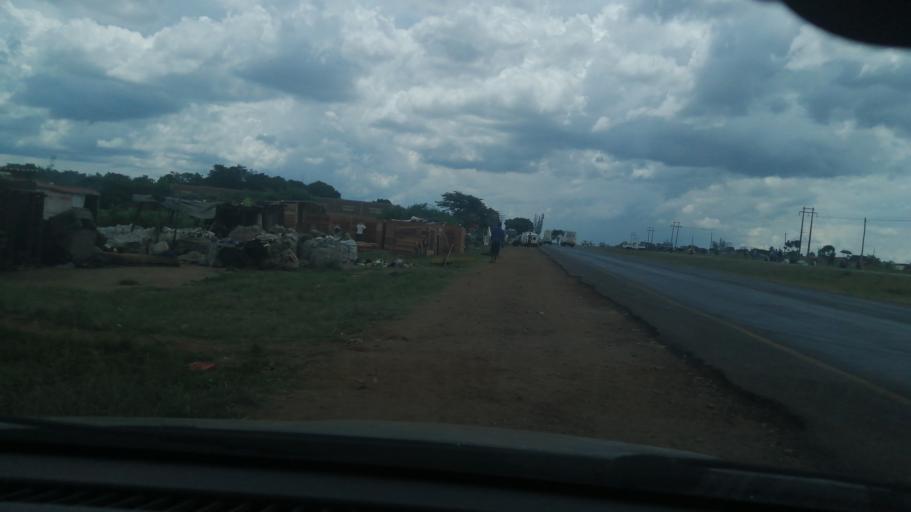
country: ZW
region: Harare
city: Harare
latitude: -17.8217
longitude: 30.8902
